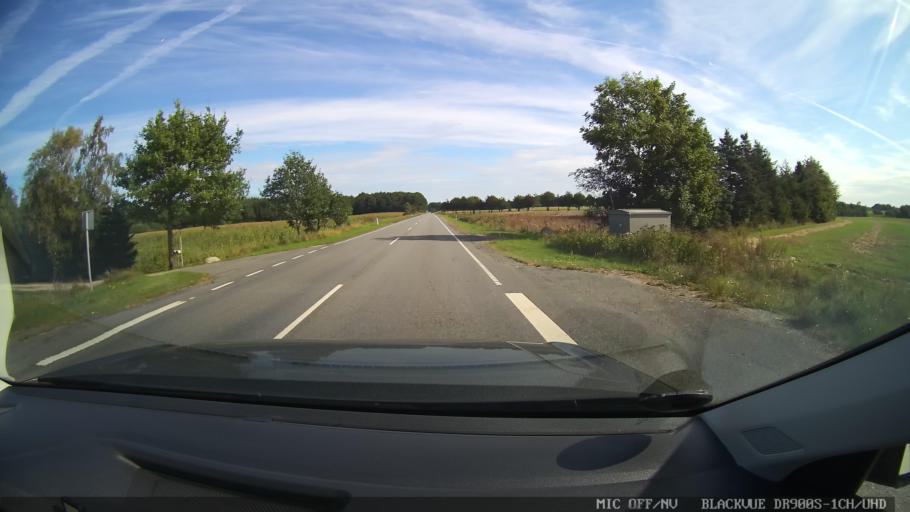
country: DK
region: North Denmark
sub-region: Mariagerfjord Kommune
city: Hadsund
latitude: 56.7841
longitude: 10.0170
